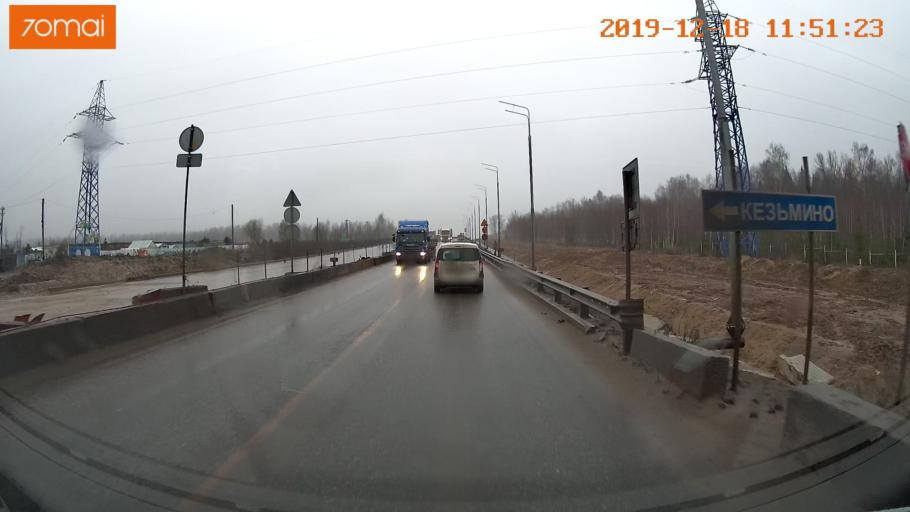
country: RU
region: Moskovskaya
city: Yershovo
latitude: 55.7929
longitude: 36.9220
